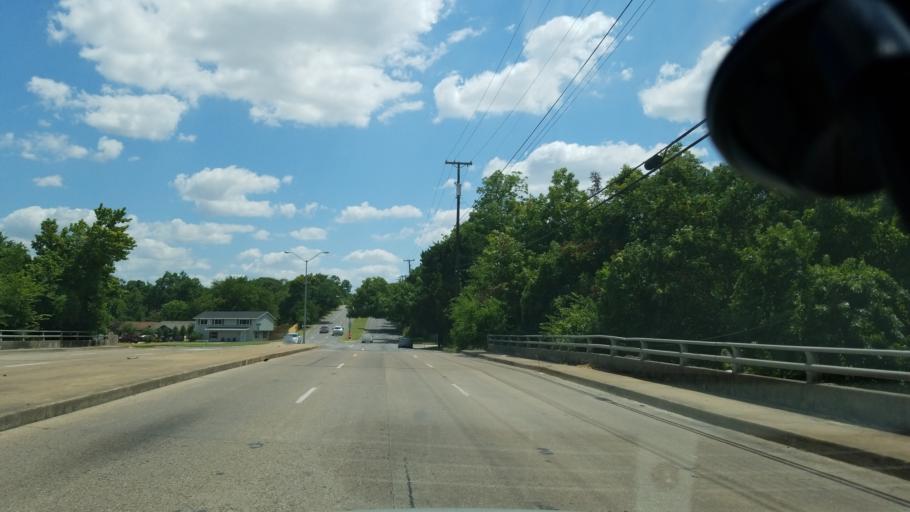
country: US
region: Texas
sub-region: Dallas County
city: Cockrell Hill
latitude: 32.7045
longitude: -96.8572
